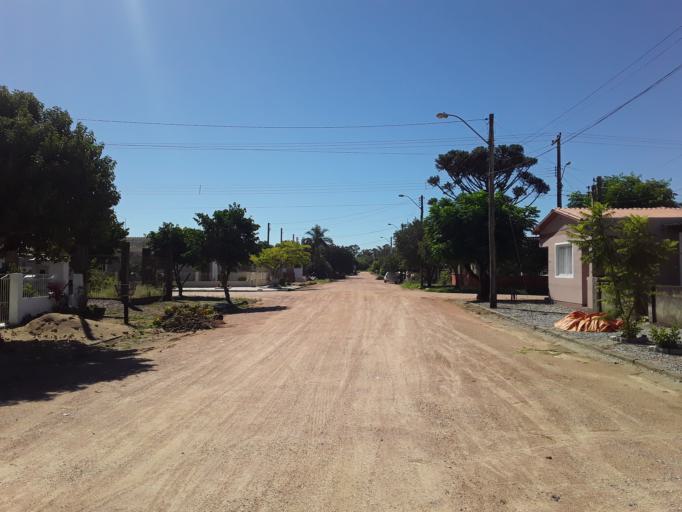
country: BR
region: Rio Grande do Sul
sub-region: Sao Lourenco Do Sul
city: Sao Lourenco do Sul
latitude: -31.3461
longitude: -51.9914
